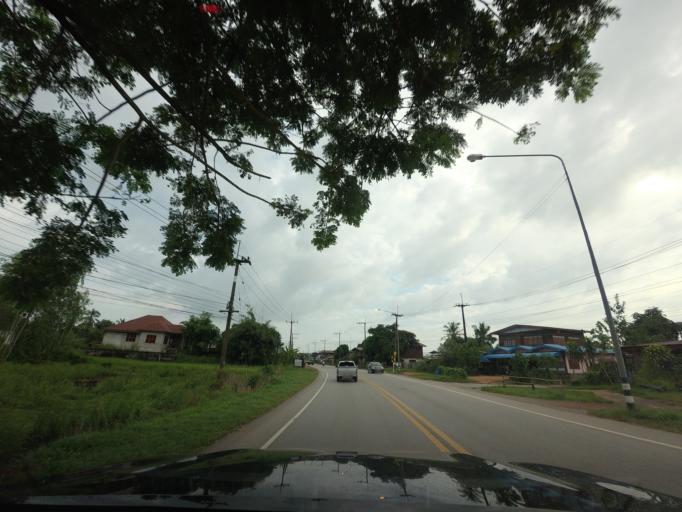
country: TH
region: Changwat Udon Thani
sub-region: Amphoe Ban Phue
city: Ban Phue
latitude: 17.7438
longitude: 102.3991
